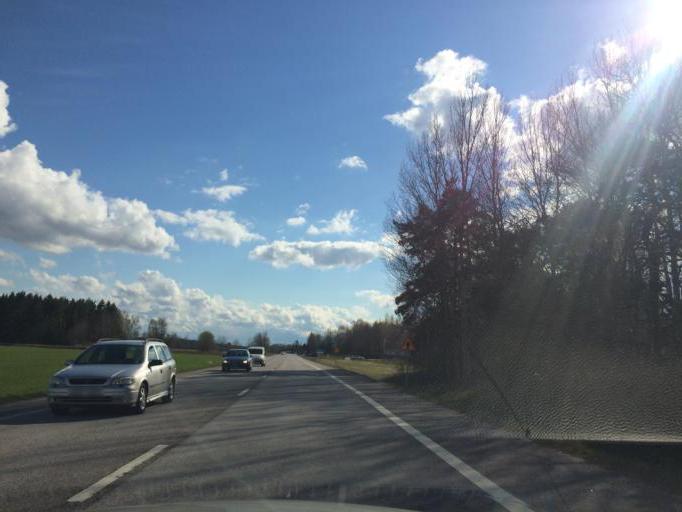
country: SE
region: Soedermanland
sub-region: Eskilstuna Kommun
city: Eskilstuna
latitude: 59.4138
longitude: 16.5850
